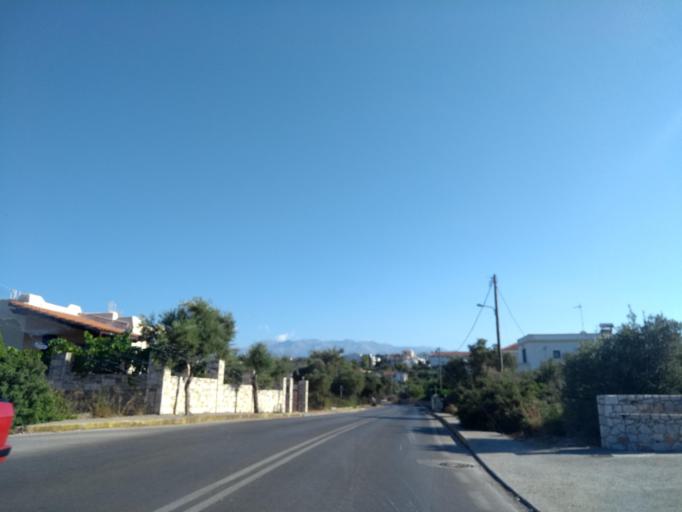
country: GR
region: Crete
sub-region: Nomos Chanias
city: Pithari
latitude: 35.5398
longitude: 24.0819
